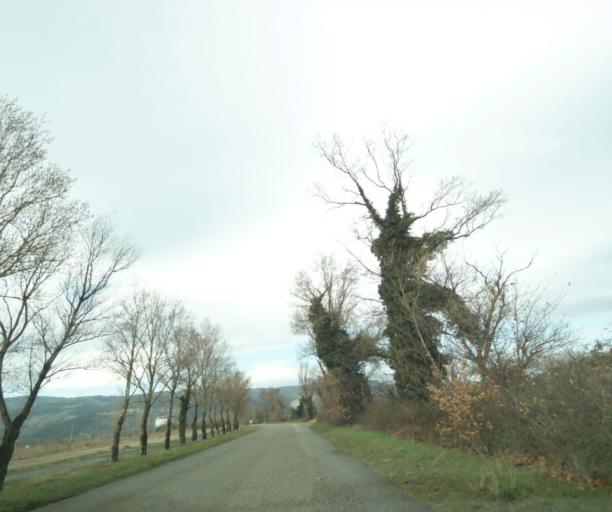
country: FR
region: Rhone-Alpes
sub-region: Departement de l'Ardeche
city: Cornas
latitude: 44.9719
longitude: 4.8702
